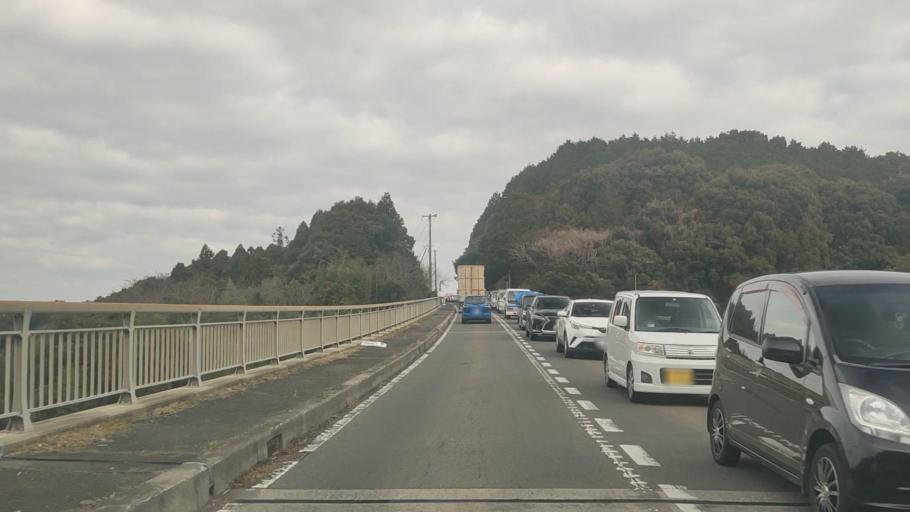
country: JP
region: Nagasaki
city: Shimabara
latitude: 32.8372
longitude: 130.2137
